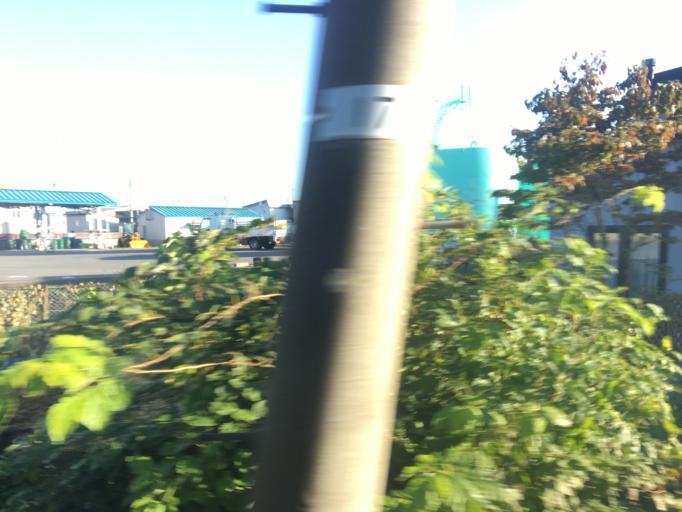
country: JP
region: Aomori
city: Hirosaki
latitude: 40.5910
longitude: 140.4909
